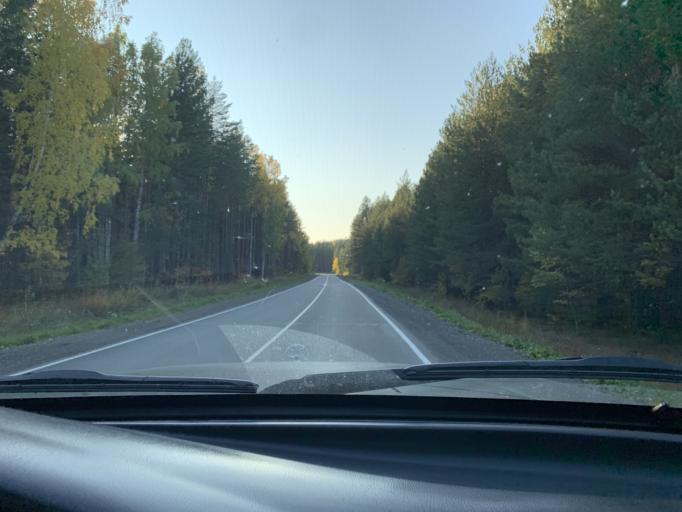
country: RU
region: Sverdlovsk
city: Verkhneye Dubrovo
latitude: 56.8676
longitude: 61.0774
